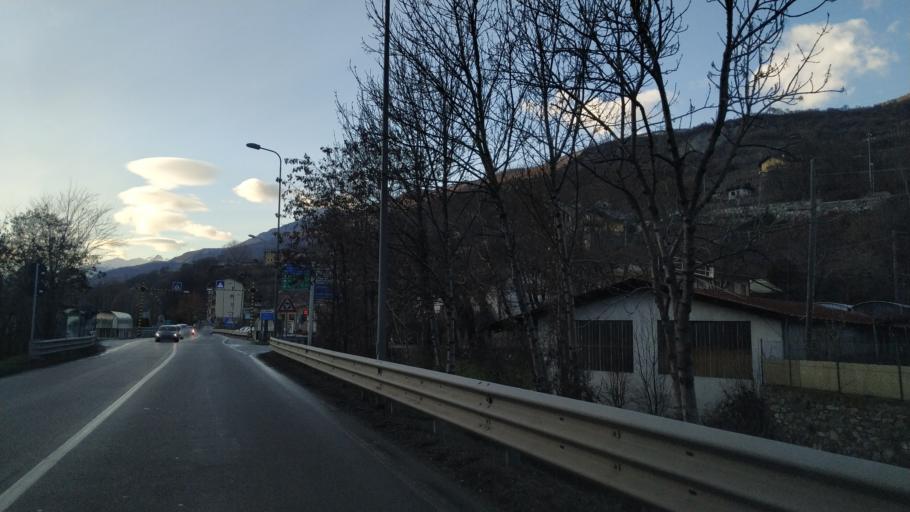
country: IT
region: Aosta Valley
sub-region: Valle d'Aosta
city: Chambave
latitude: 45.7435
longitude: 7.5463
